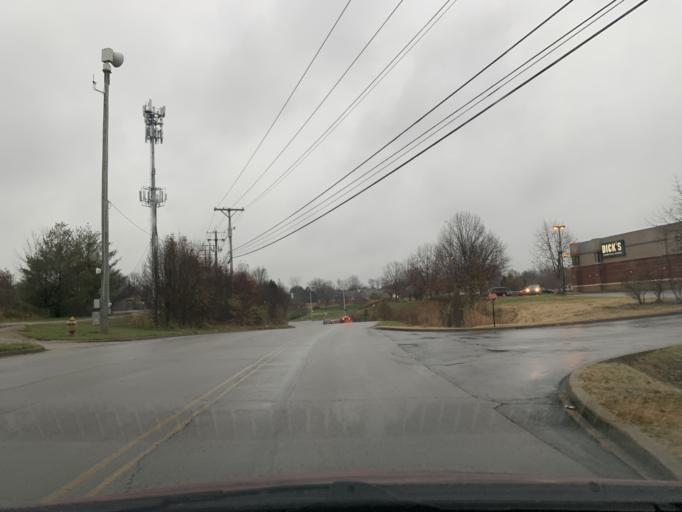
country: US
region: Kentucky
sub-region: Jefferson County
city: Hurstbourne Acres
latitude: 38.1989
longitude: -85.6052
